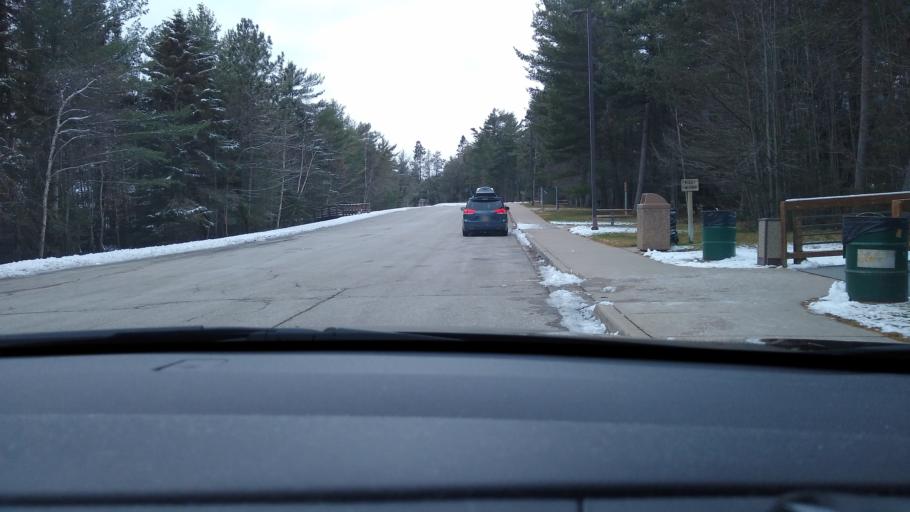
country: US
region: Michigan
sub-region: Luce County
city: Newberry
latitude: 46.0950
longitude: -85.3916
